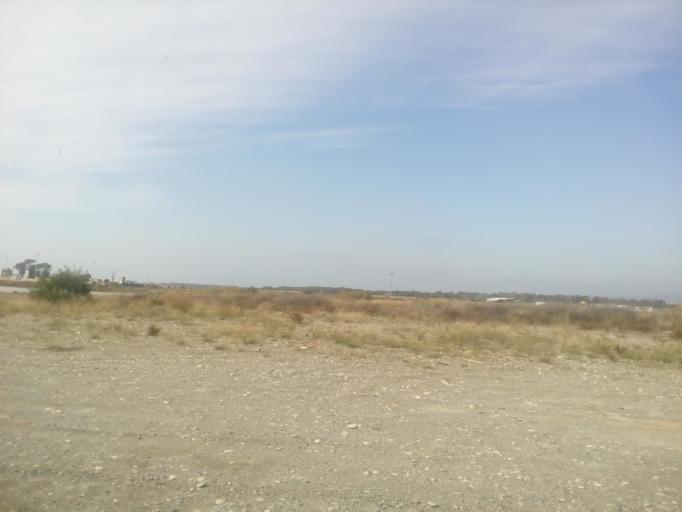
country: CY
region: Limassol
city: Limassol
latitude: 34.6418
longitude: 33.0108
